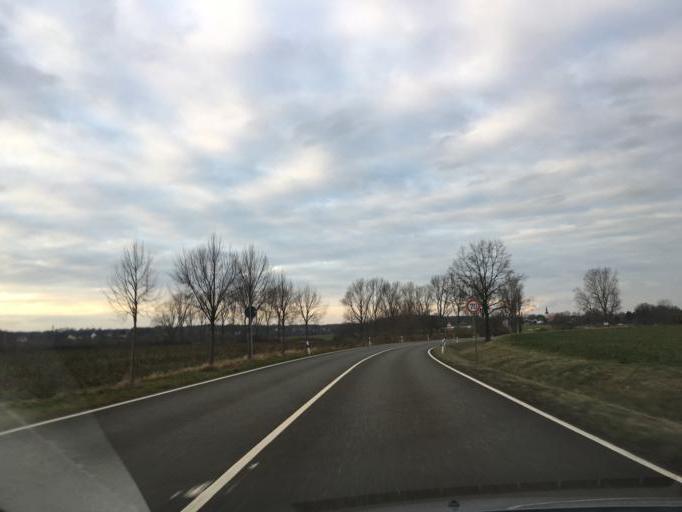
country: DE
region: Thuringia
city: Fockendorf
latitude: 51.0415
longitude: 12.4565
